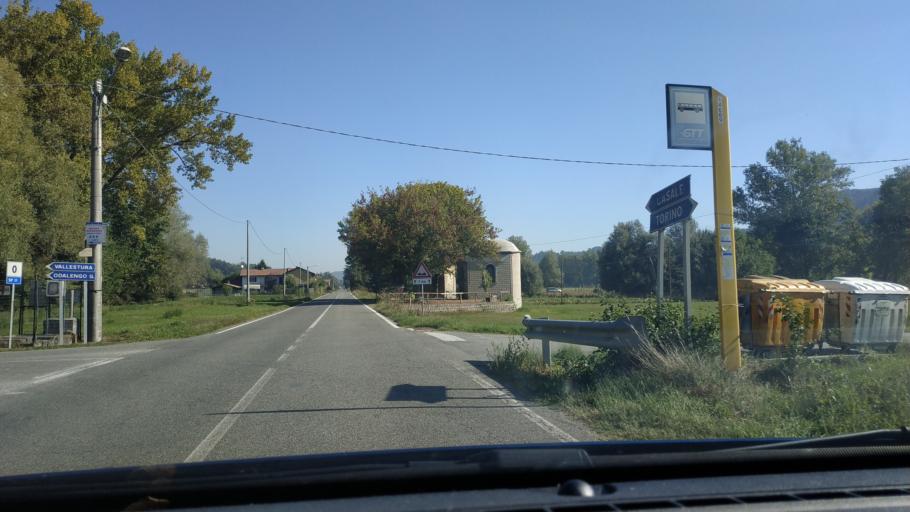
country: IT
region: Piedmont
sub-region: Provincia di Alessandria
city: Odalengo Grande
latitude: 45.0946
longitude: 8.1856
